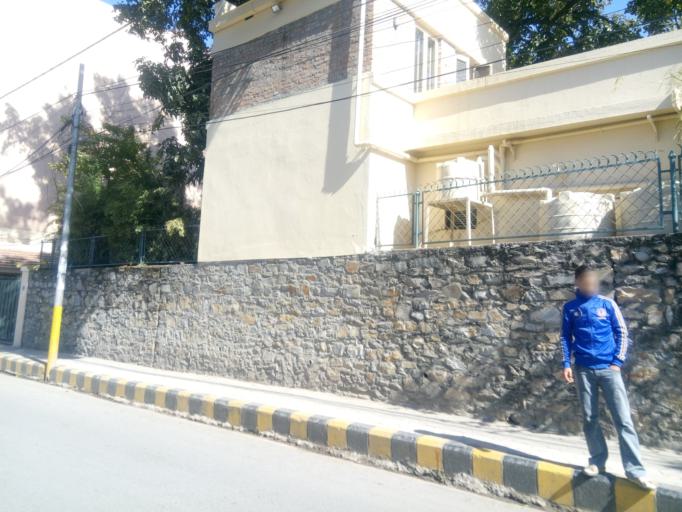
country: NP
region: Central Region
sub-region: Bagmati Zone
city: Kathmandu
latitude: 27.7203
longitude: 85.3314
